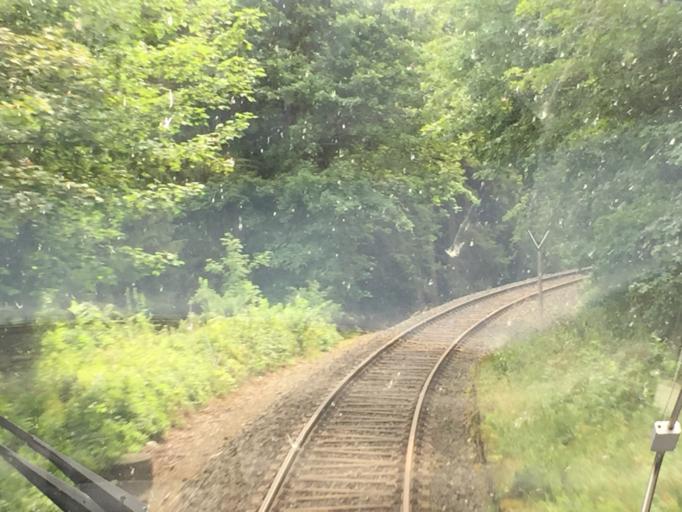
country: DE
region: Hesse
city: Willingen
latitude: 51.2819
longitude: 8.6336
